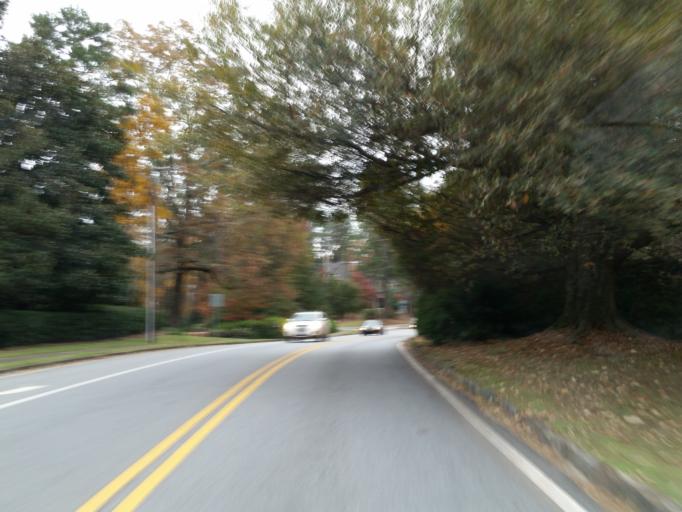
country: US
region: Georgia
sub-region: Fulton County
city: Sandy Springs
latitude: 33.8927
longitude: -84.3920
